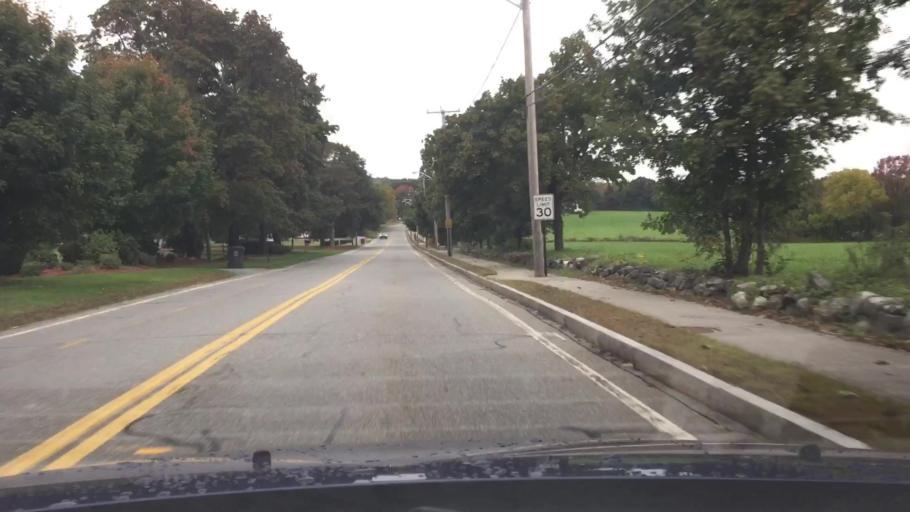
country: US
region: Massachusetts
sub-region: Middlesex County
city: Dracut
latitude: 42.6681
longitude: -71.3501
